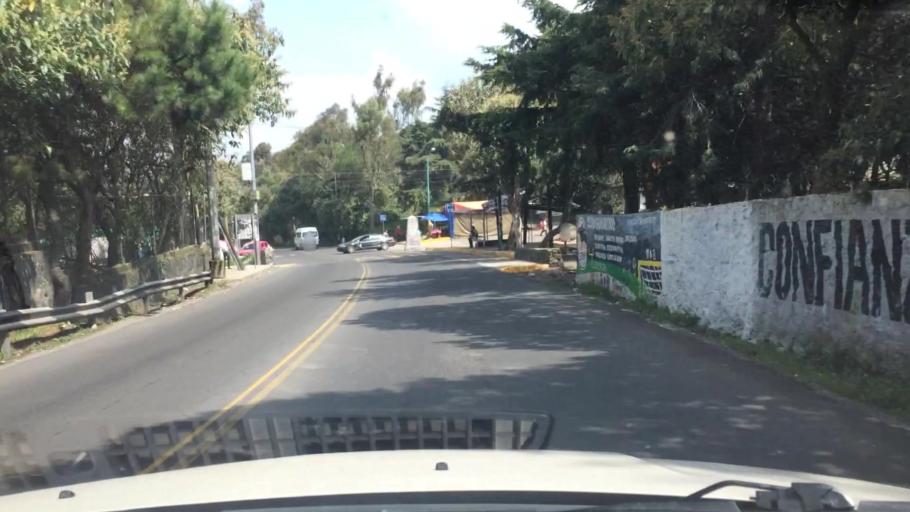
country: MX
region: Mexico City
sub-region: Tlalpan
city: Lomas de Tepemecatl
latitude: 19.2661
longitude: -99.2286
